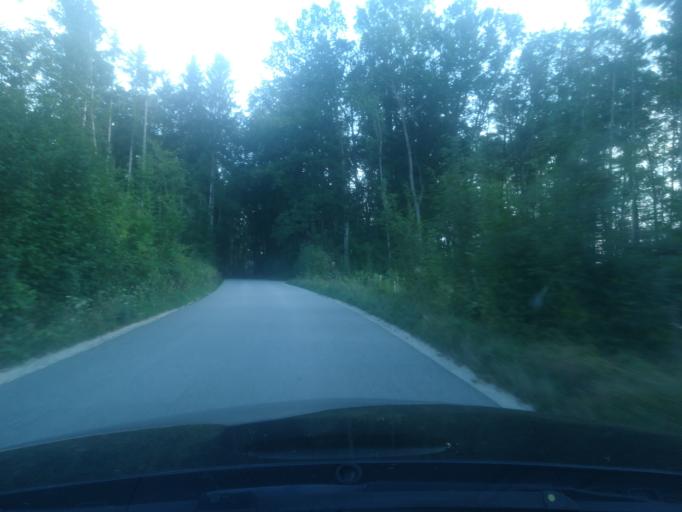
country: AT
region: Upper Austria
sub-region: Wels-Land
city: Marchtrenk
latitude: 48.1615
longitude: 14.1682
